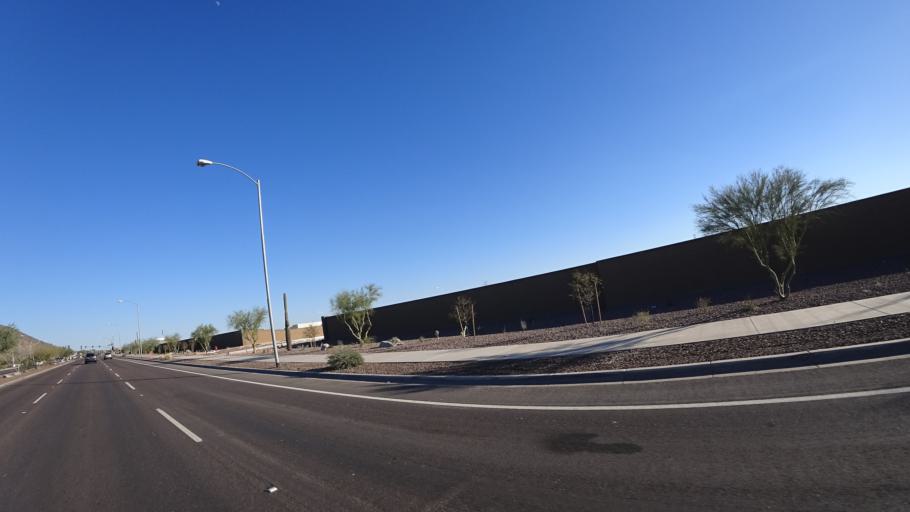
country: US
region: Arizona
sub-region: Maricopa County
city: Sun City West
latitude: 33.7106
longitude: -112.2668
